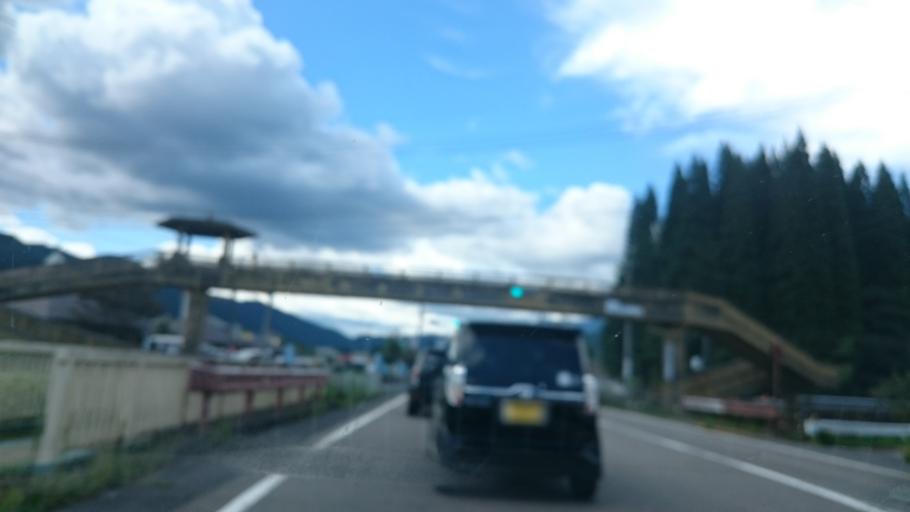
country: JP
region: Gifu
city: Nakatsugawa
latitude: 35.6423
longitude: 137.4424
